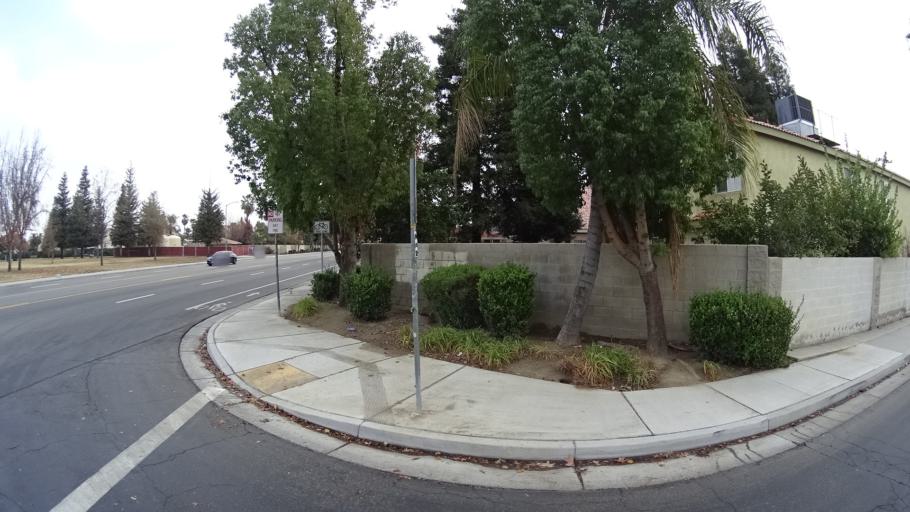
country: US
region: California
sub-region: Kern County
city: Greenfield
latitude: 35.3031
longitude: -119.0726
